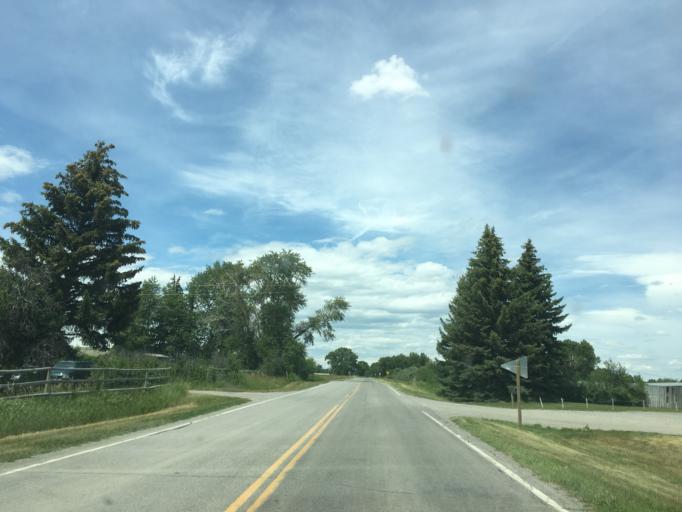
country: US
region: Montana
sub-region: Teton County
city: Choteau
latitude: 47.8272
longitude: -112.1958
